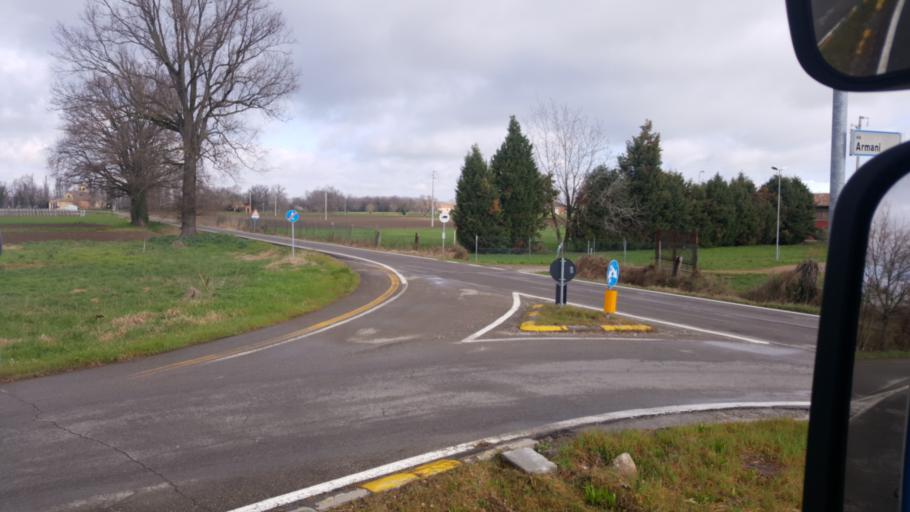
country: IT
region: Emilia-Romagna
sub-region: Provincia di Reggio Emilia
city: Fellegara
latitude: 44.6134
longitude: 10.7038
